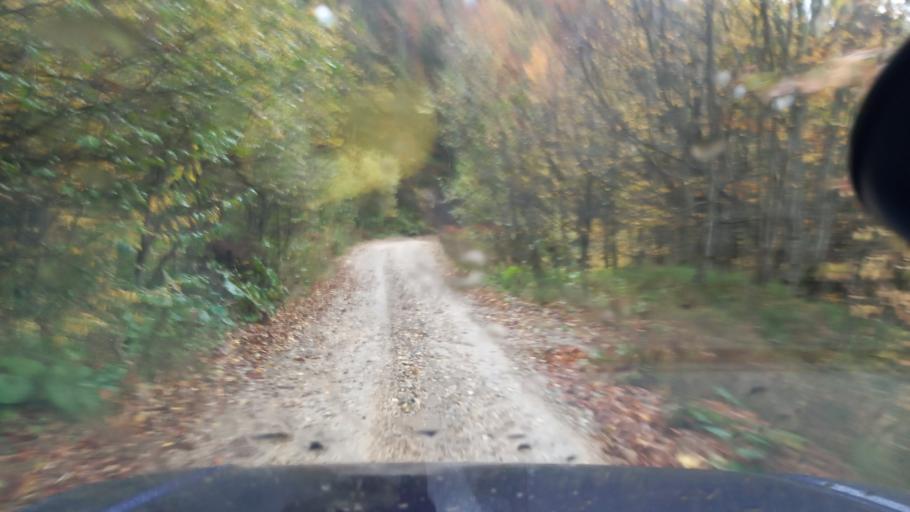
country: RU
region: Krasnodarskiy
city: Neftegorsk
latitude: 44.0345
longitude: 39.8366
